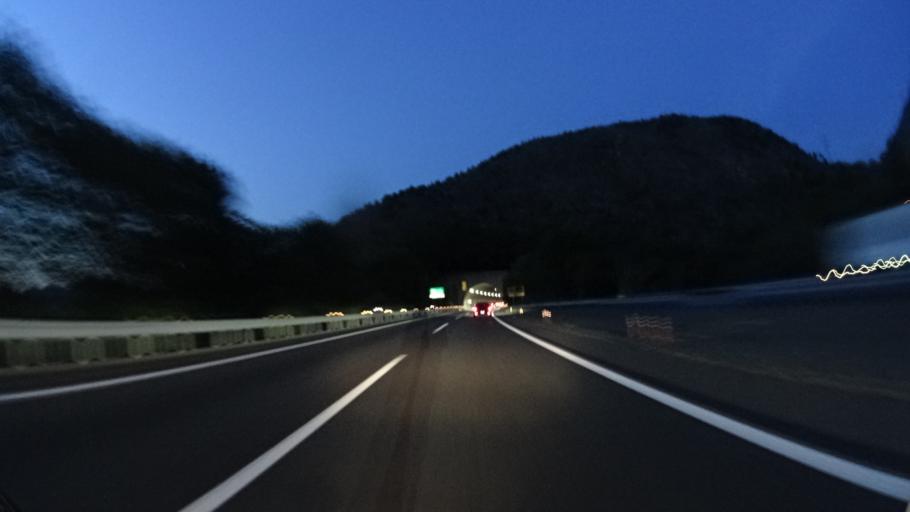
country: JP
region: Hyogo
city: Kariya
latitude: 34.7867
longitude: 134.3995
